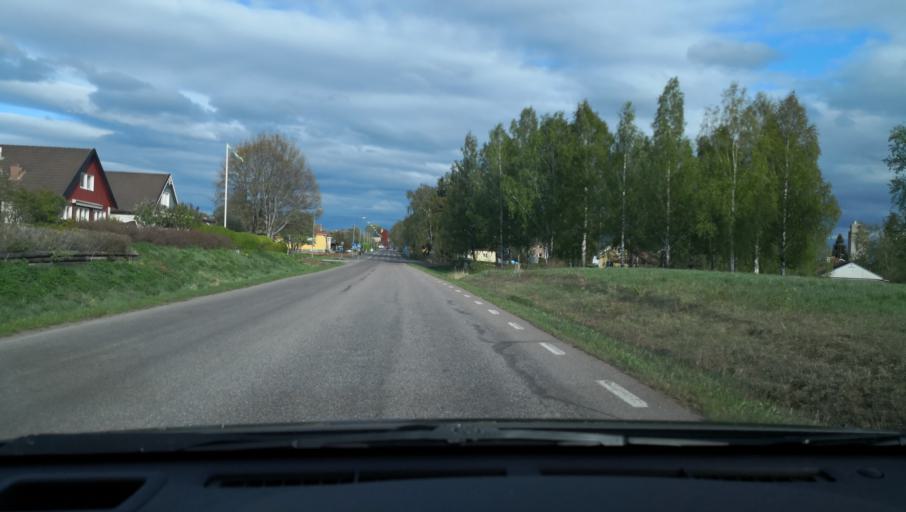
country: SE
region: Dalarna
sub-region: Hedemora Kommun
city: Hedemora
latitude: 60.2795
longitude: 15.9705
